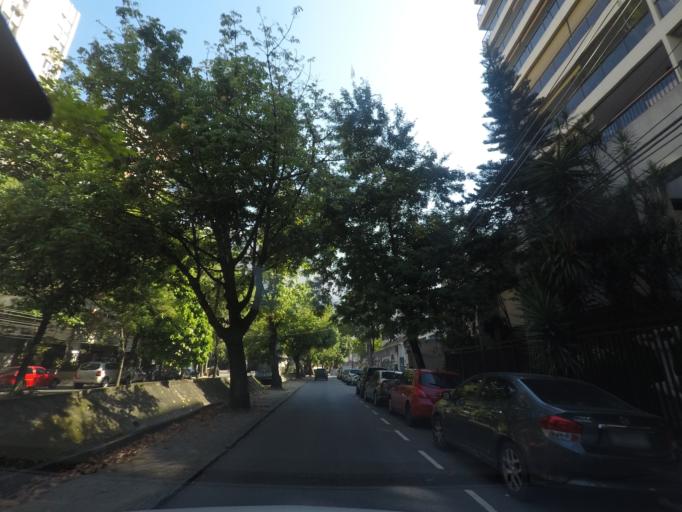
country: BR
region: Rio de Janeiro
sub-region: Rio De Janeiro
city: Rio de Janeiro
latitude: -22.9658
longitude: -43.2172
